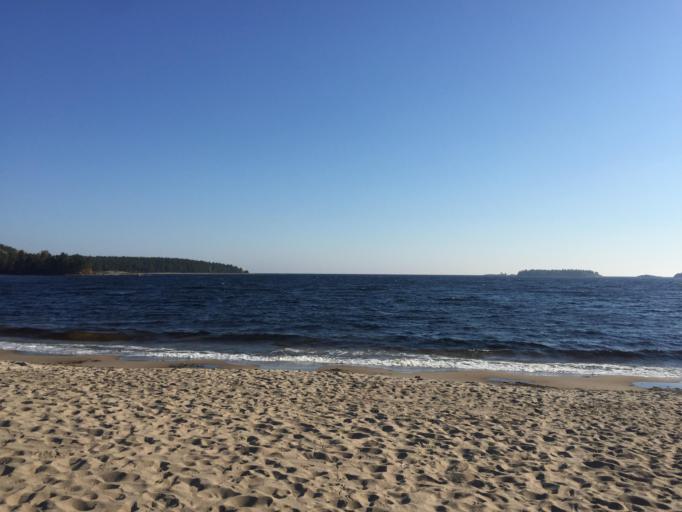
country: RU
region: Leningrad
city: Priozersk
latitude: 61.2792
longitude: 30.1003
